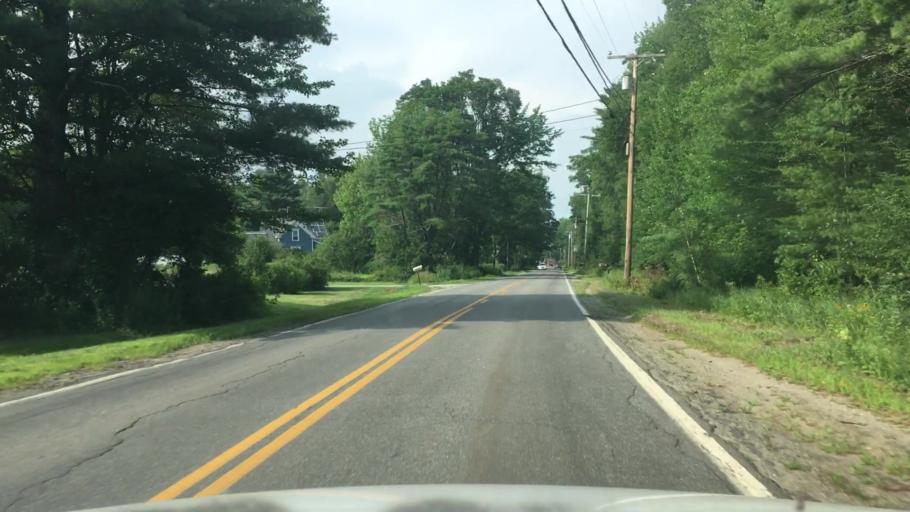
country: US
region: Maine
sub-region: Lincoln County
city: Waldoboro
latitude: 44.1135
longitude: -69.3659
